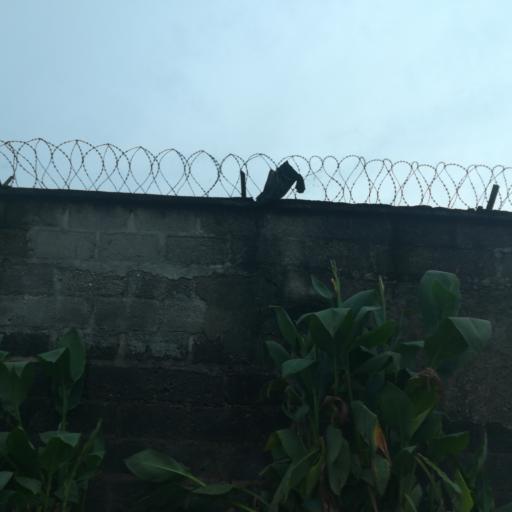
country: NG
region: Rivers
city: Port Harcourt
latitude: 4.7561
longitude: 7.0110
